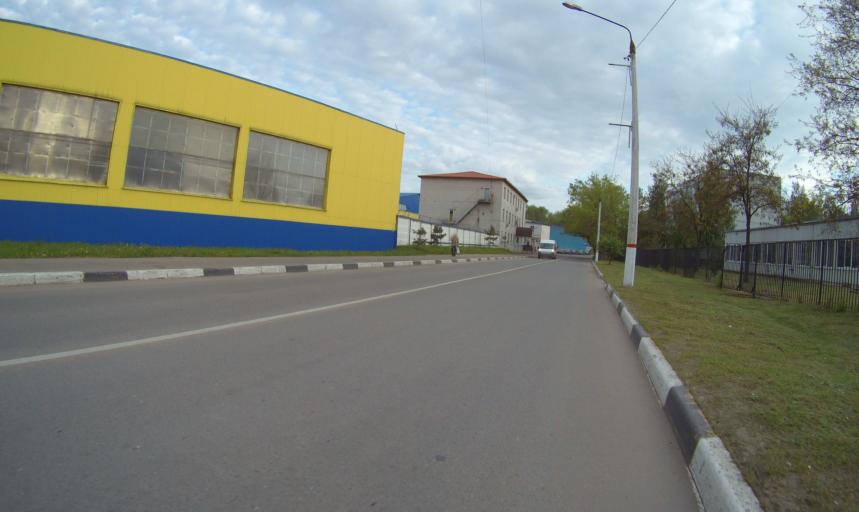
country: RU
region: Moskovskaya
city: Ramenskoye
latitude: 55.5721
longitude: 38.2466
